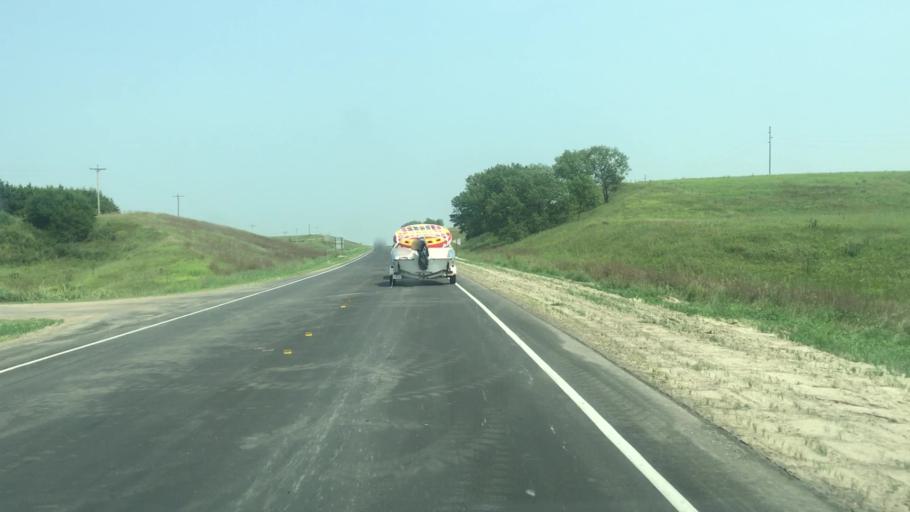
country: US
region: Nebraska
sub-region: Sherman County
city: Loup City
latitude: 41.2628
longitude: -98.9366
